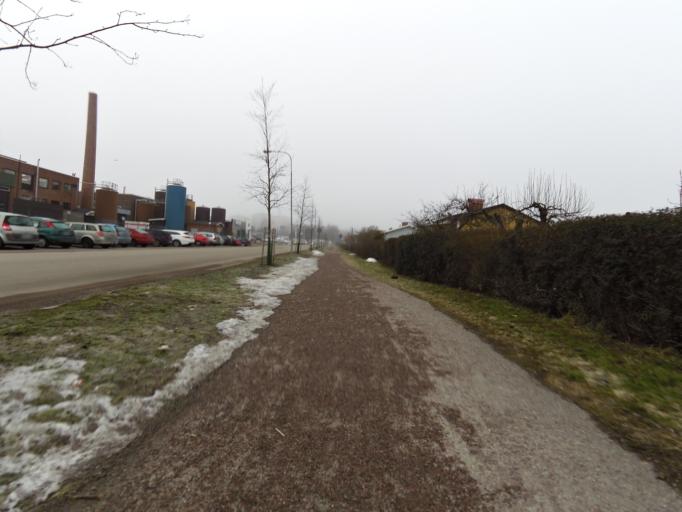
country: SE
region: Gaevleborg
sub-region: Gavle Kommun
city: Gavle
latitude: 60.6633
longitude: 17.1545
